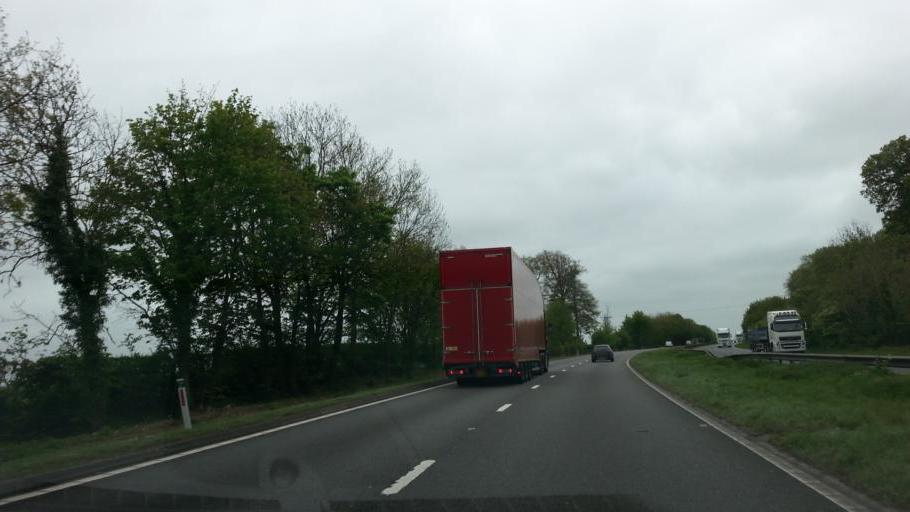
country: GB
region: England
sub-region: Lincolnshire
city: Grantham
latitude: 52.8516
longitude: -0.6267
